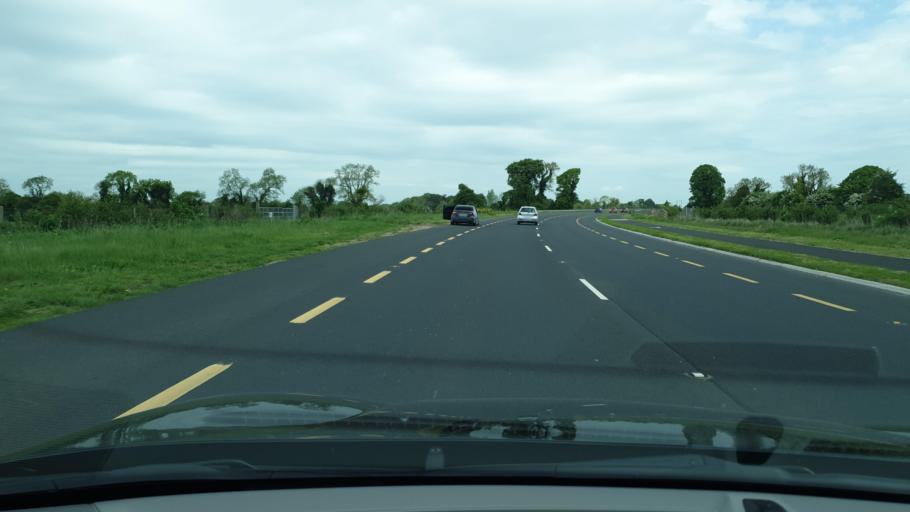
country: IE
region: Leinster
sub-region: Kildare
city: Sallins
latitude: 53.2550
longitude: -6.6808
